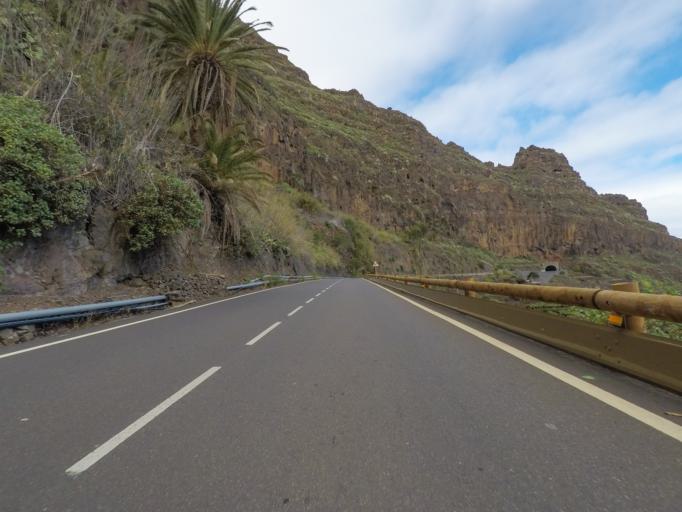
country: ES
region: Canary Islands
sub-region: Provincia de Santa Cruz de Tenerife
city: Agulo
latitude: 28.1882
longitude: -17.1978
